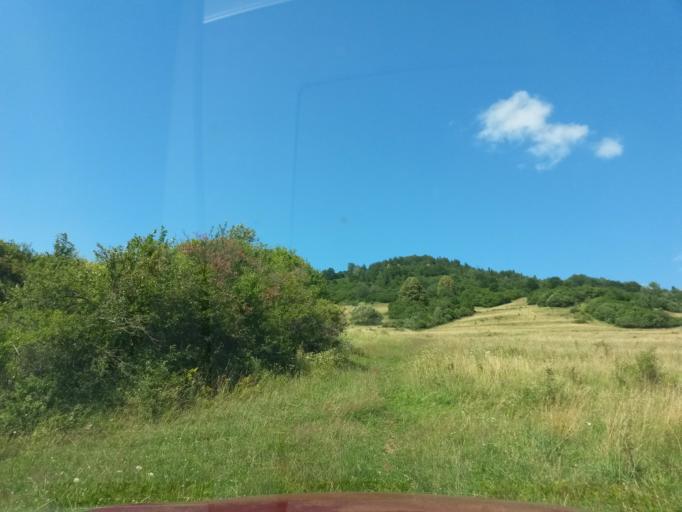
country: SK
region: Kosicky
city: Spisska Nova Ves
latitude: 48.8456
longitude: 20.6210
